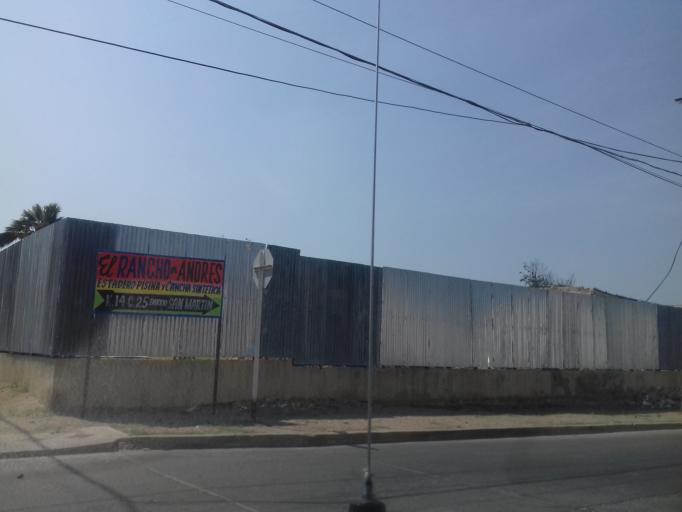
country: CO
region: La Guajira
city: Maicao
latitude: 11.3812
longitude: -72.2417
